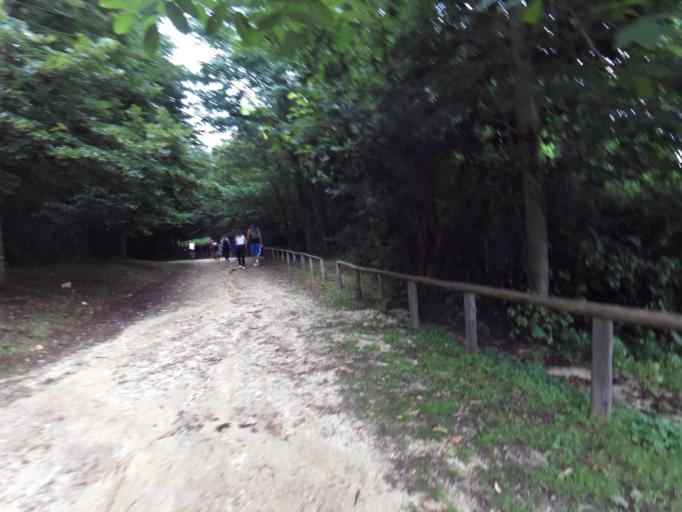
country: IT
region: Calabria
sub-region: Provincia di Vibo-Valentia
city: Serra San Bruno
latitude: 38.5606
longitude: 16.3165
